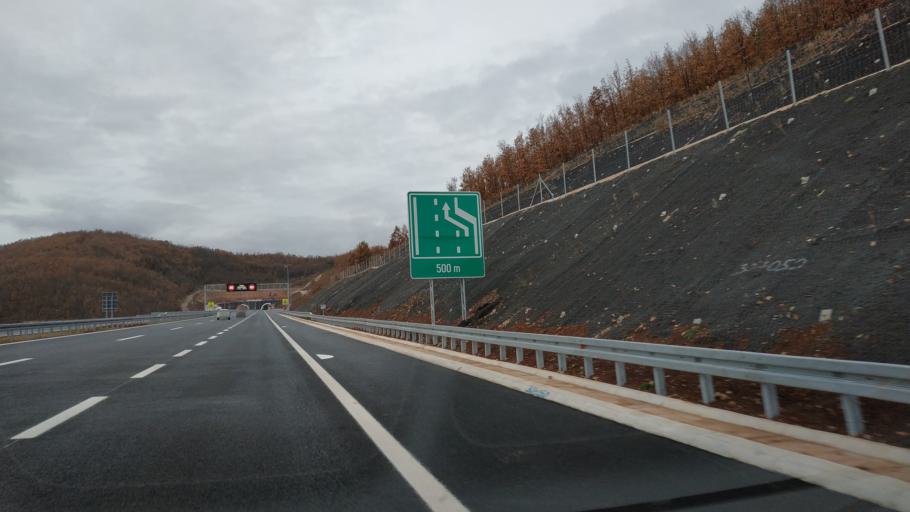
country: RS
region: Central Serbia
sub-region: Nisavski Okrug
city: Gadzin Han
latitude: 43.2628
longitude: 22.1444
